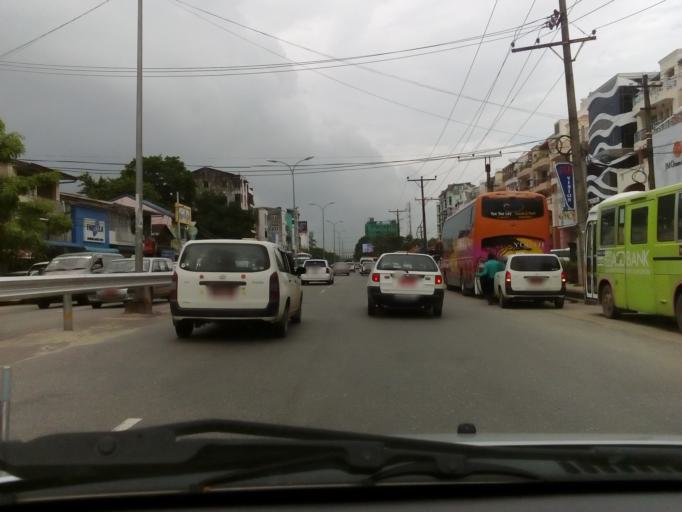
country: MM
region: Yangon
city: Yangon
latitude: 16.8151
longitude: 96.1687
